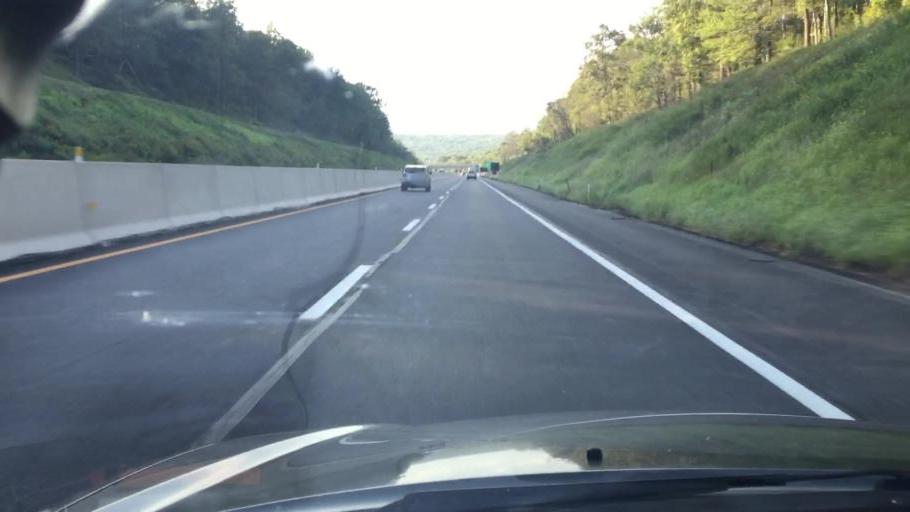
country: US
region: Pennsylvania
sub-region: Luzerne County
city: White Haven
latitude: 41.0630
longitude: -75.6882
